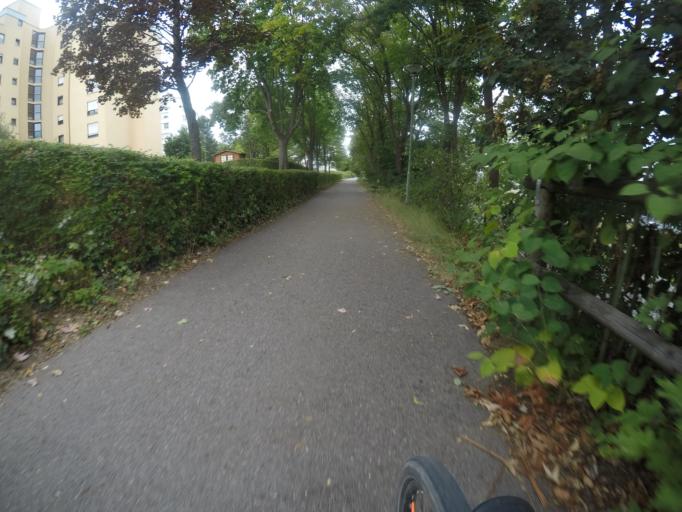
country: DE
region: Baden-Wuerttemberg
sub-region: Karlsruhe Region
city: Eutingen
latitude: 48.8857
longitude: 8.7384
